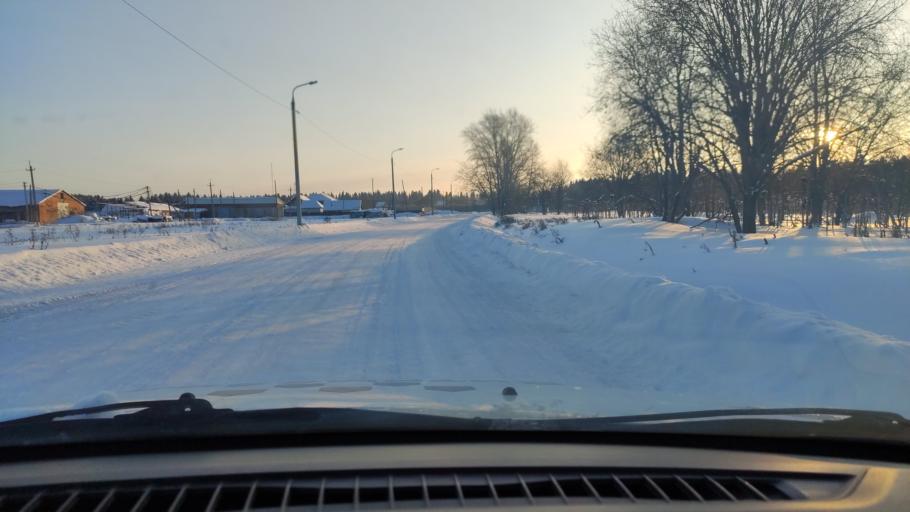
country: RU
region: Perm
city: Sylva
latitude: 58.0410
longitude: 56.7250
